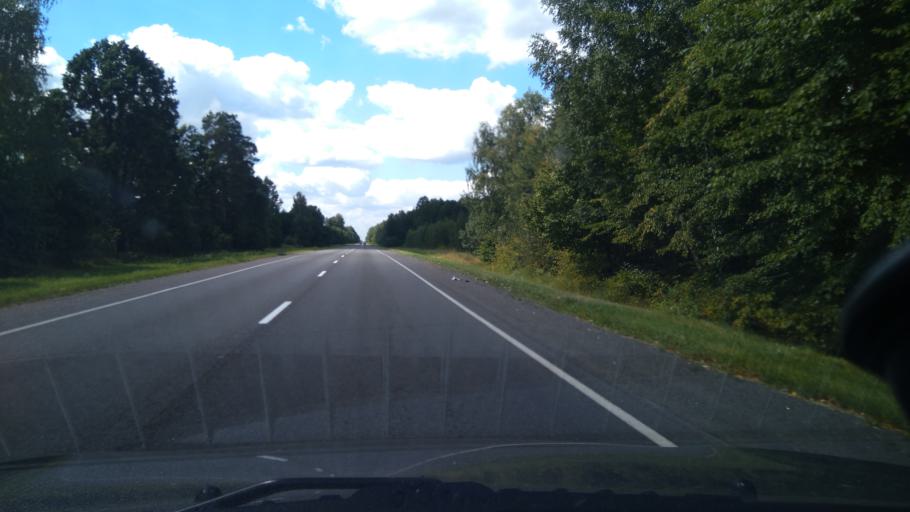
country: BY
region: Brest
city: Nyakhachava
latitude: 52.6703
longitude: 25.2587
